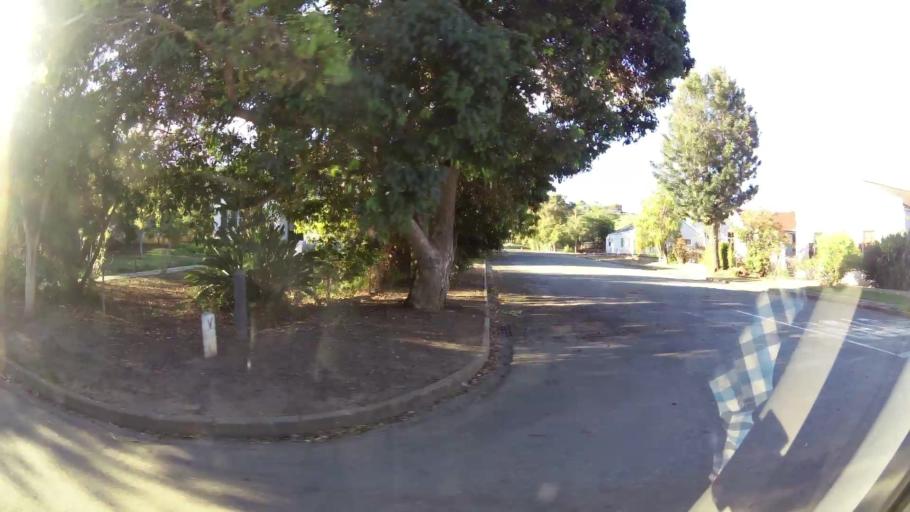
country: ZA
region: Western Cape
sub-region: Eden District Municipality
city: Riversdale
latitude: -34.0878
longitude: 20.9542
